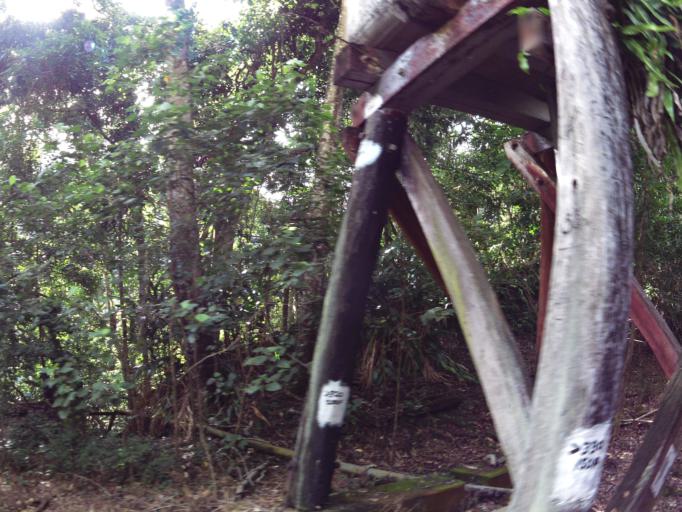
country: AU
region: Queensland
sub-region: Cairns
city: Redlynch
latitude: -16.8798
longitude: 145.6535
